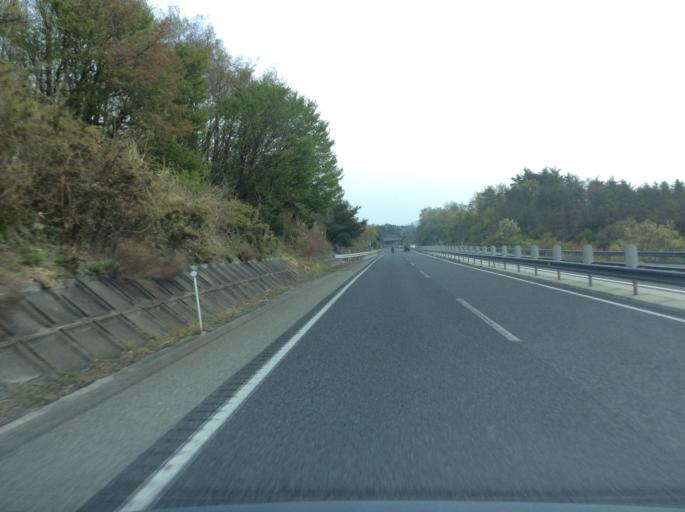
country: JP
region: Fukushima
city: Funehikimachi-funehiki
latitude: 37.4184
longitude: 140.5606
